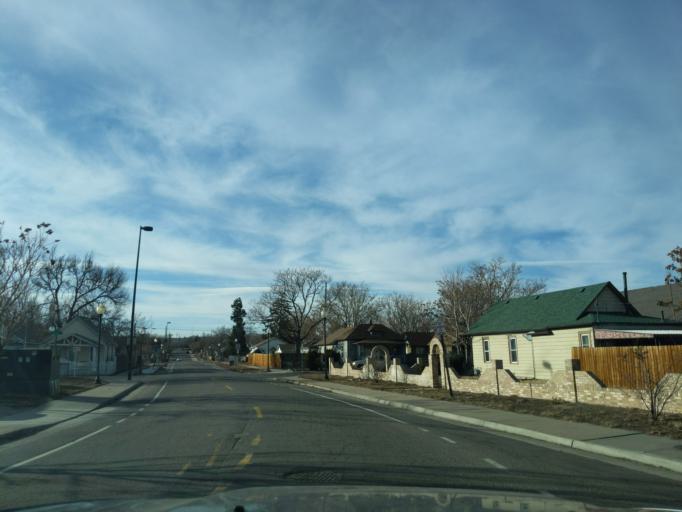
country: US
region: Colorado
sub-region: Denver County
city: Denver
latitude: 39.7819
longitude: -104.9829
